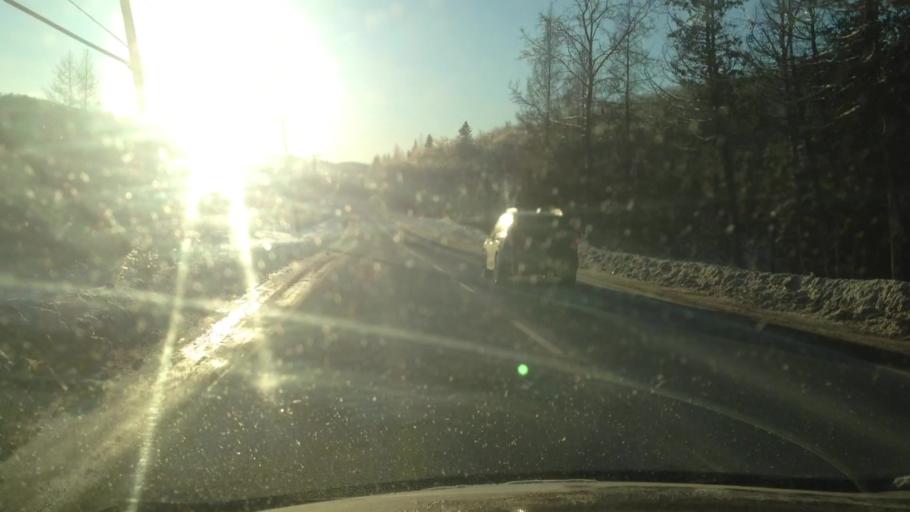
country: CA
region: Quebec
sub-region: Laurentides
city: Saint-Sauveur
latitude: 45.9065
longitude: -74.2997
